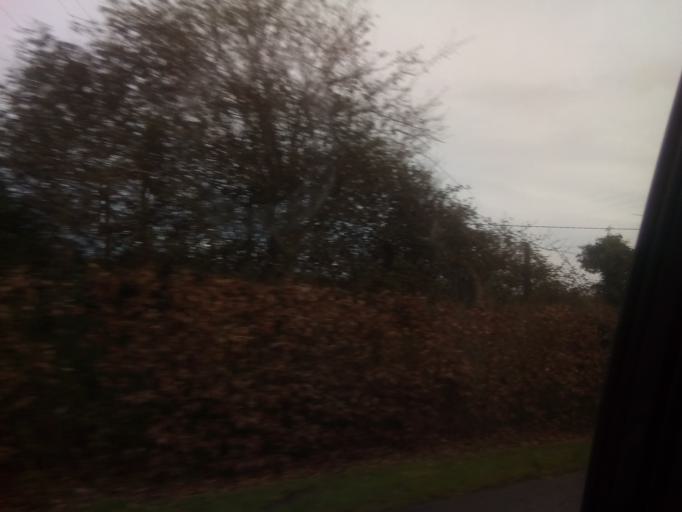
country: IE
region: Leinster
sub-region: Laois
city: Abbeyleix
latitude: 52.8498
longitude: -7.3911
